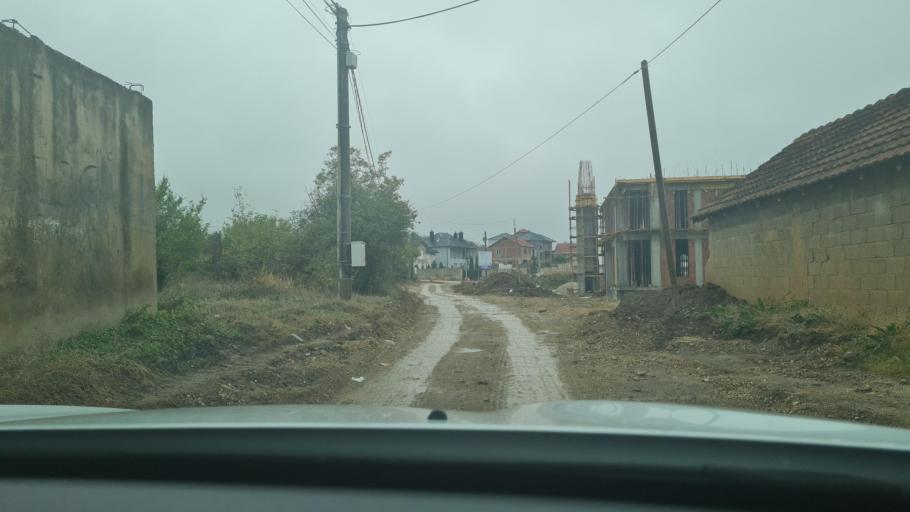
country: MK
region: Opstina Lipkovo
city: Matejche
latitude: 42.1201
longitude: 21.6033
